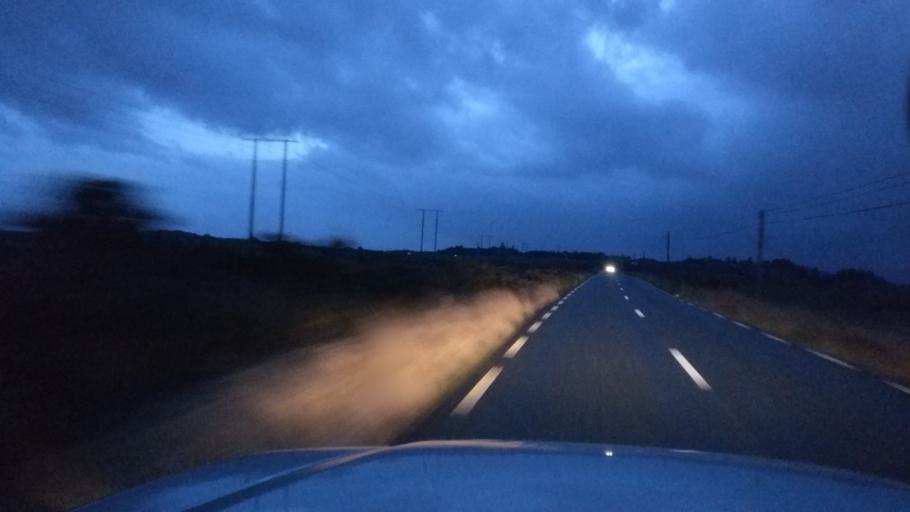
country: IE
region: Connaught
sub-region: County Galway
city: Oughterard
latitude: 53.3980
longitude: -9.5454
